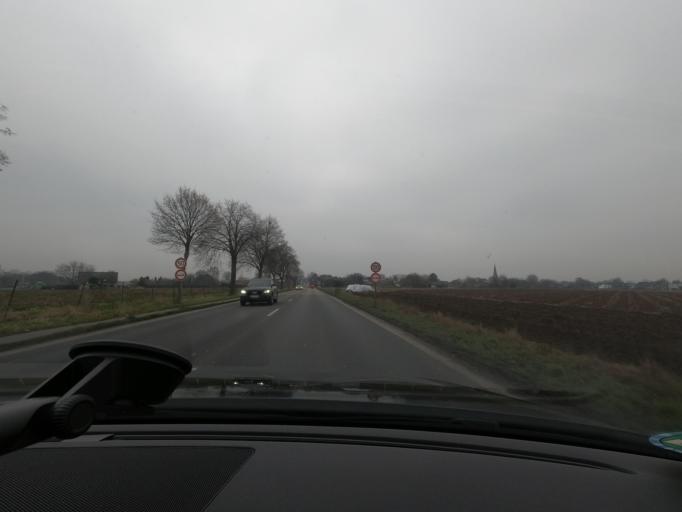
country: NL
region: Limburg
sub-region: Gemeente Venlo
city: Venlo
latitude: 51.3341
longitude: 6.2164
